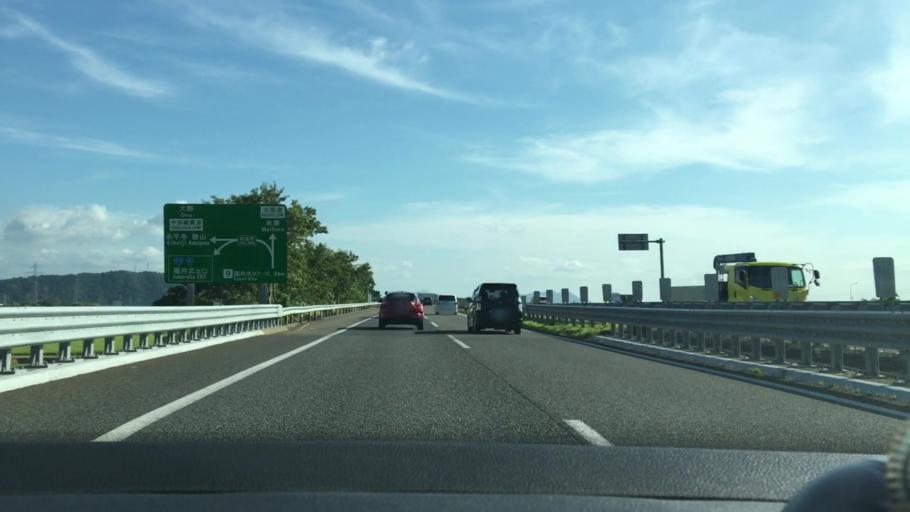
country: JP
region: Fukui
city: Maruoka
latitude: 36.1056
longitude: 136.2808
